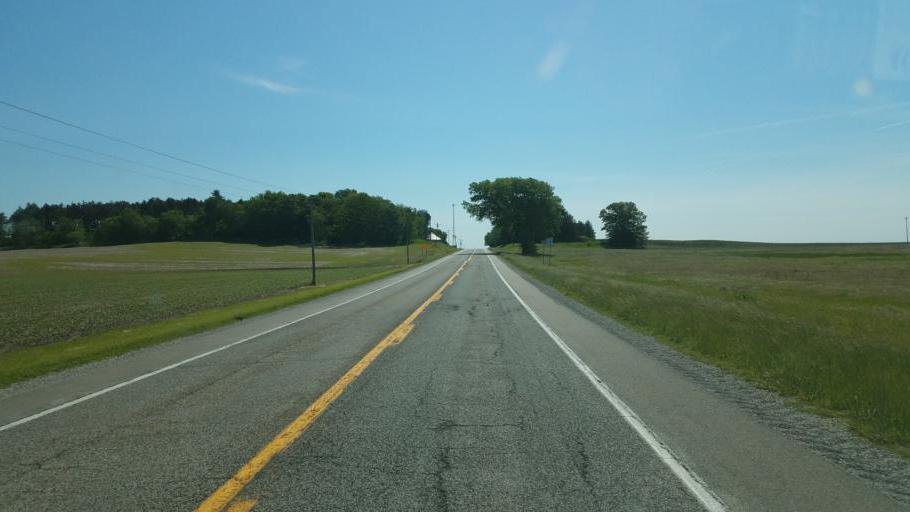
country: US
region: Illinois
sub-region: Mason County
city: Manito
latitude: 40.3035
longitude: -89.7842
